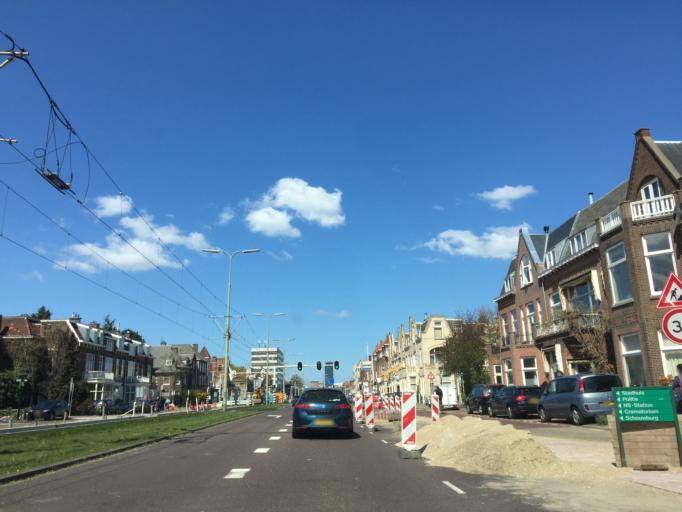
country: NL
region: South Holland
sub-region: Gemeente Rijswijk
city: Rijswijk
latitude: 52.0546
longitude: 4.3400
